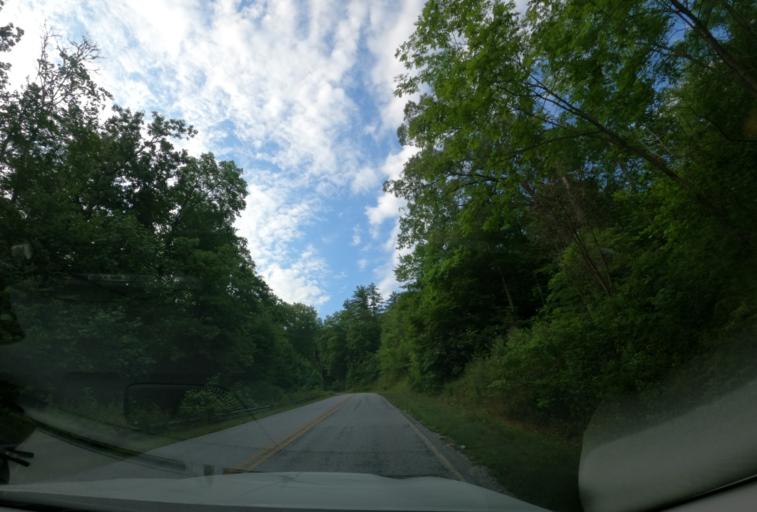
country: US
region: North Carolina
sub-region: Transylvania County
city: Brevard
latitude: 35.1798
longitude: -82.9338
